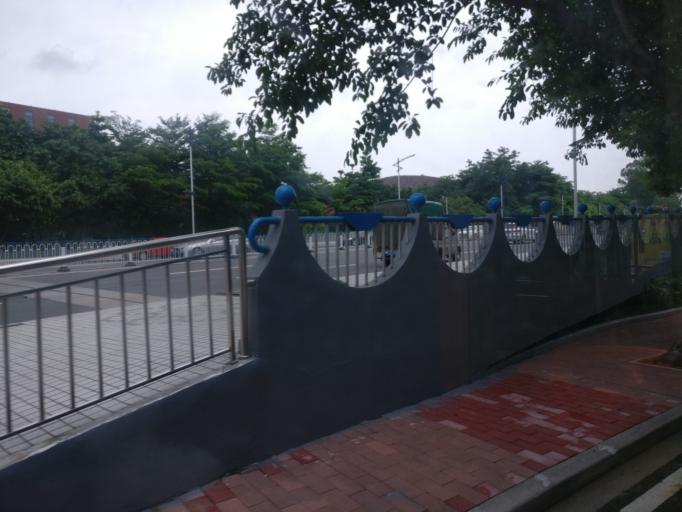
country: CN
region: Guangdong
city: Huangshi
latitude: 23.1882
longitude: 113.2753
